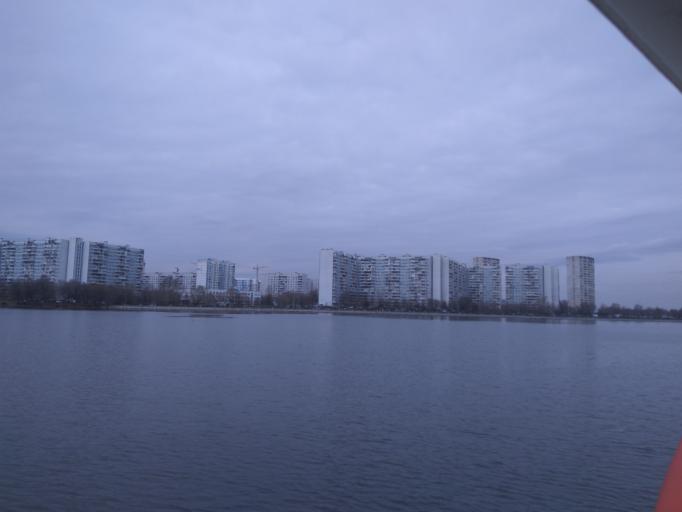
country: RU
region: Moscow
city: Mar'ino
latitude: 55.6790
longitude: 37.7133
